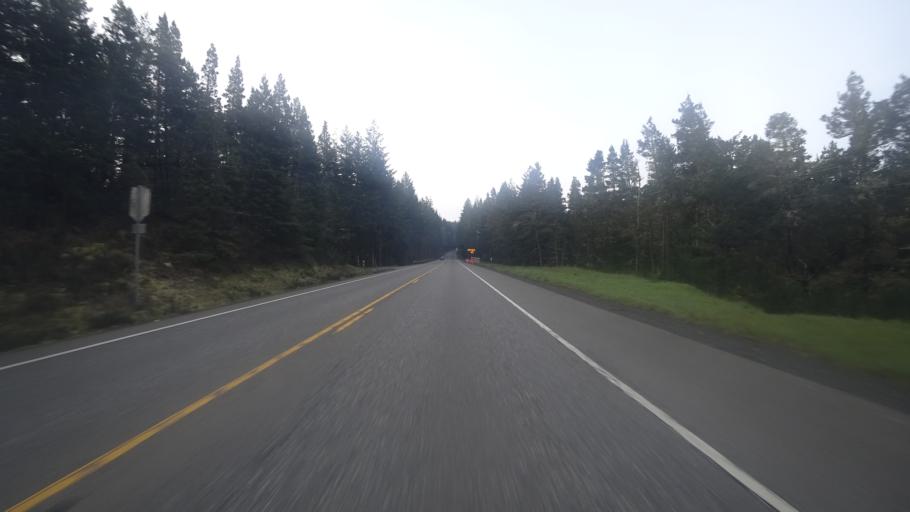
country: US
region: Oregon
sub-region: Coos County
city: Lakeside
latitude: 43.6273
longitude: -124.1830
